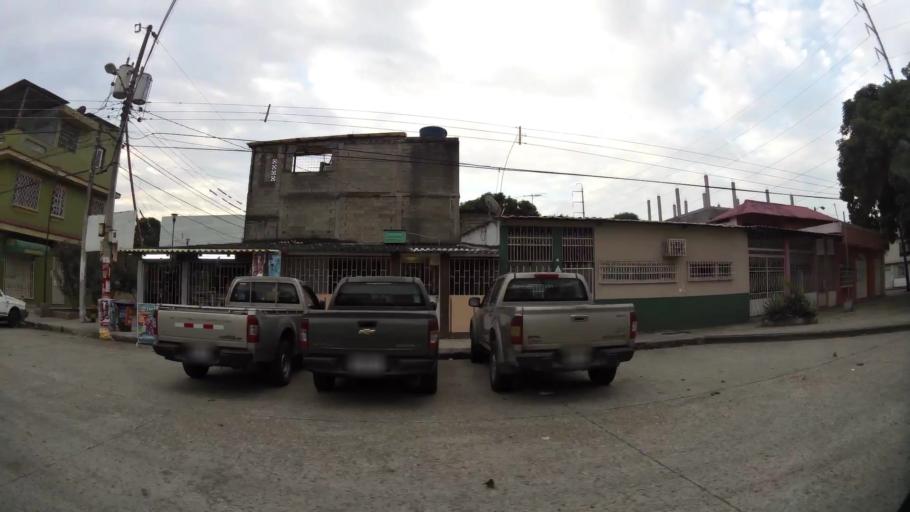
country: EC
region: Guayas
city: Guayaquil
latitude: -2.2397
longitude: -79.8877
